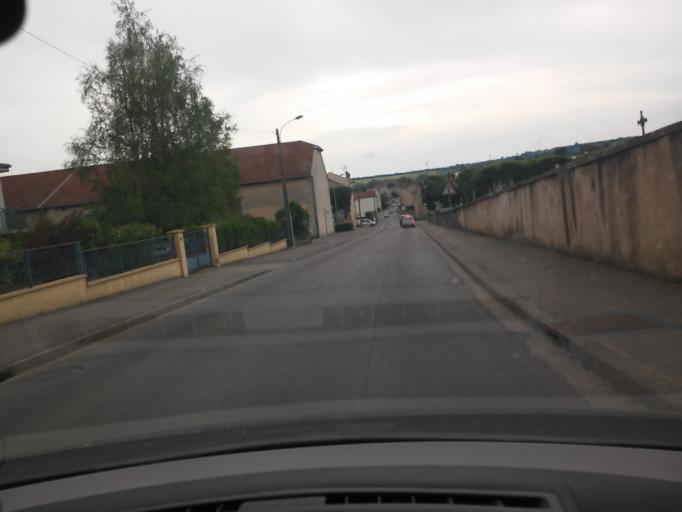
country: FR
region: Lorraine
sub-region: Departement de la Meuse
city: Commercy
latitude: 48.7598
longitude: 5.5824
